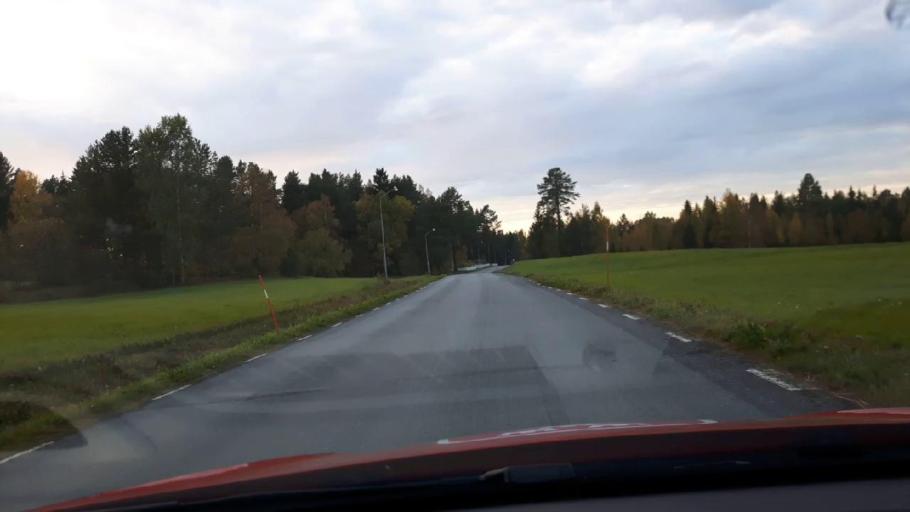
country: SE
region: Jaemtland
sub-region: OEstersunds Kommun
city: Lit
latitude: 63.3127
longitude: 14.9907
